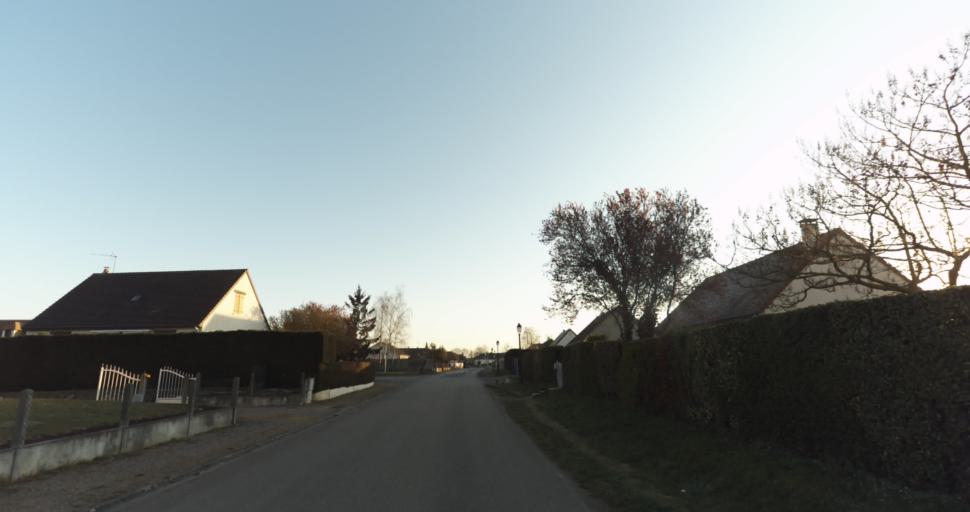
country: FR
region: Lower Normandy
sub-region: Departement du Calvados
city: Saint-Pierre-sur-Dives
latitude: 49.0326
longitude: -0.0294
